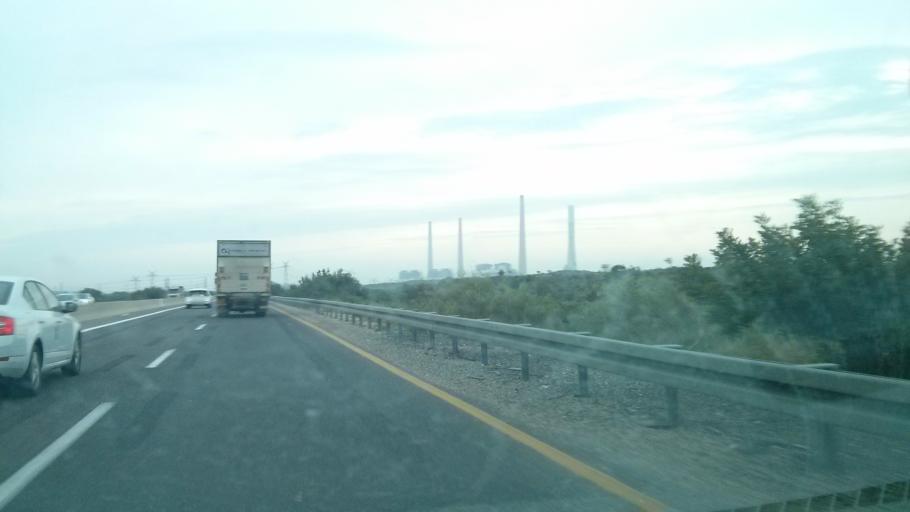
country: IL
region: Haifa
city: Qesarya
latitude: 32.4843
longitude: 34.9125
